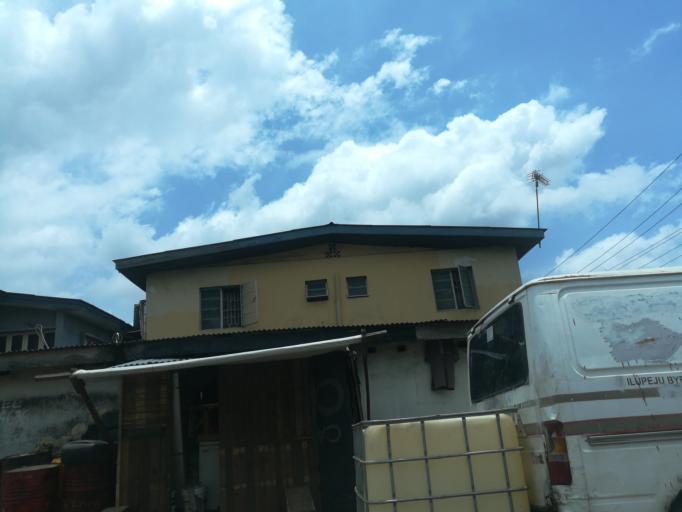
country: NG
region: Lagos
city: Somolu
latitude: 6.5479
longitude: 3.3581
